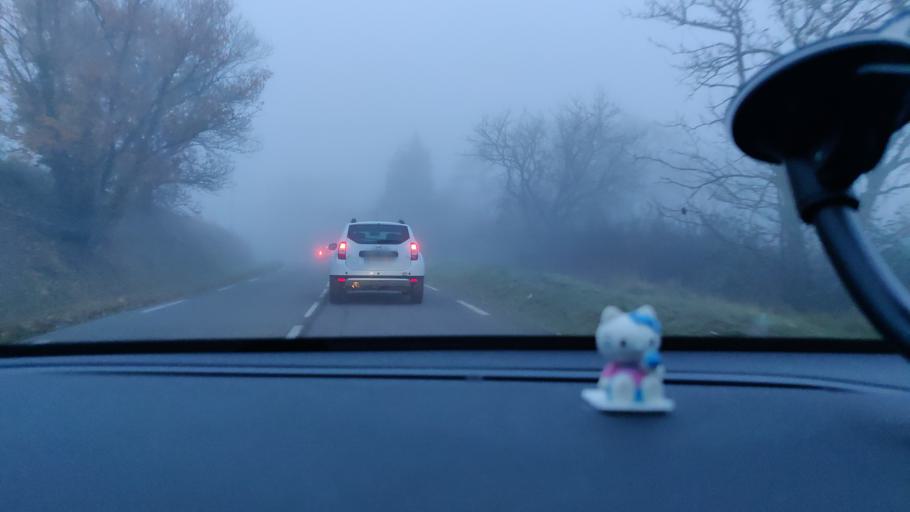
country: FR
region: Midi-Pyrenees
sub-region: Departement de la Haute-Garonne
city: Vieille-Toulouse
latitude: 43.5182
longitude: 1.4631
